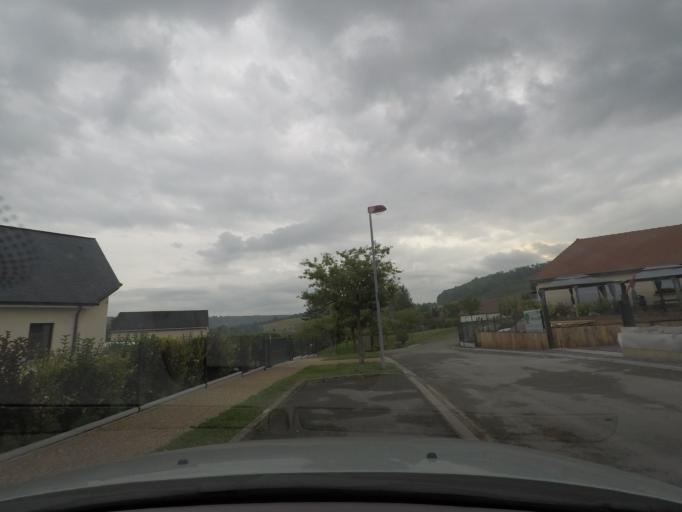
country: FR
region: Haute-Normandie
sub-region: Departement de la Seine-Maritime
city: Neufchatel-en-Bray
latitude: 49.7298
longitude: 1.4461
